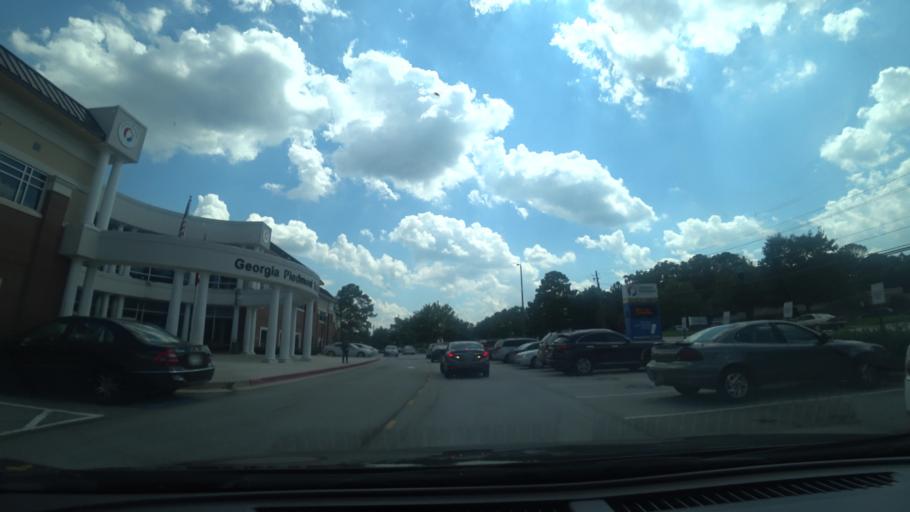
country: US
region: Georgia
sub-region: DeKalb County
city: Clarkston
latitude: 33.7900
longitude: -84.2359
